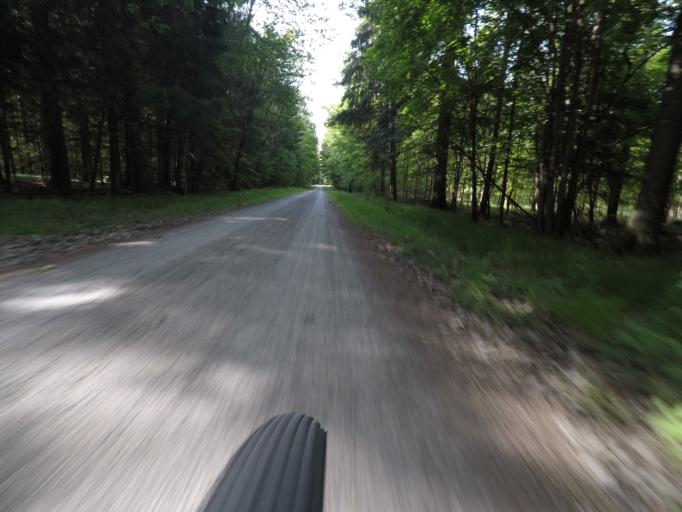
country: DE
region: Baden-Wuerttemberg
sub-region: Regierungsbezirk Stuttgart
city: Weil im Schonbuch
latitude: 48.5825
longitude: 9.0585
